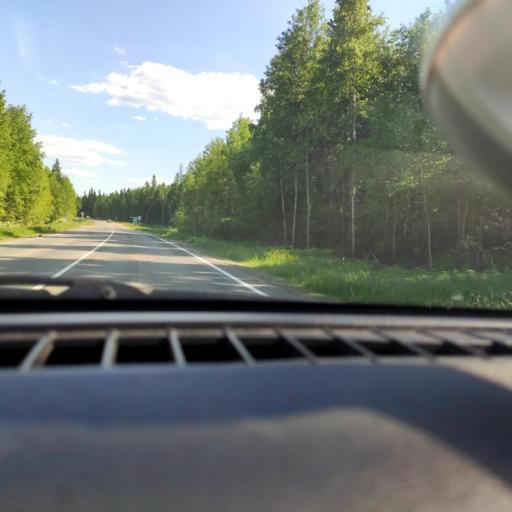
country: RU
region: Perm
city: Perm
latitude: 58.2221
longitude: 56.1661
